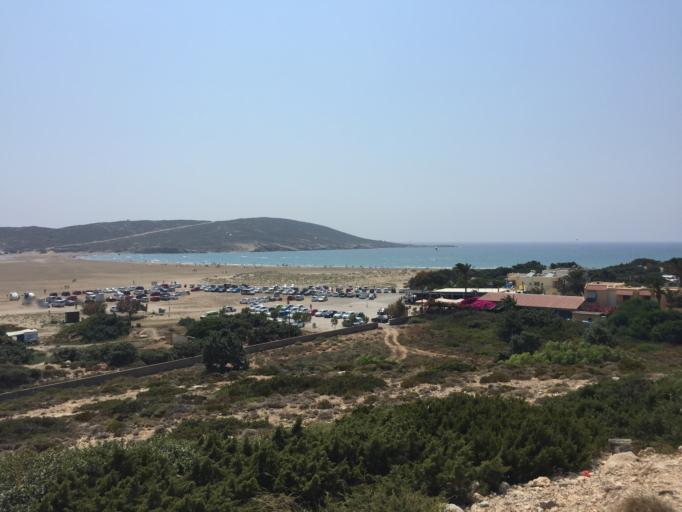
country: GR
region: South Aegean
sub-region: Nomos Dodekanisou
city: Lardos
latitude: 35.8916
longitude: 27.7751
